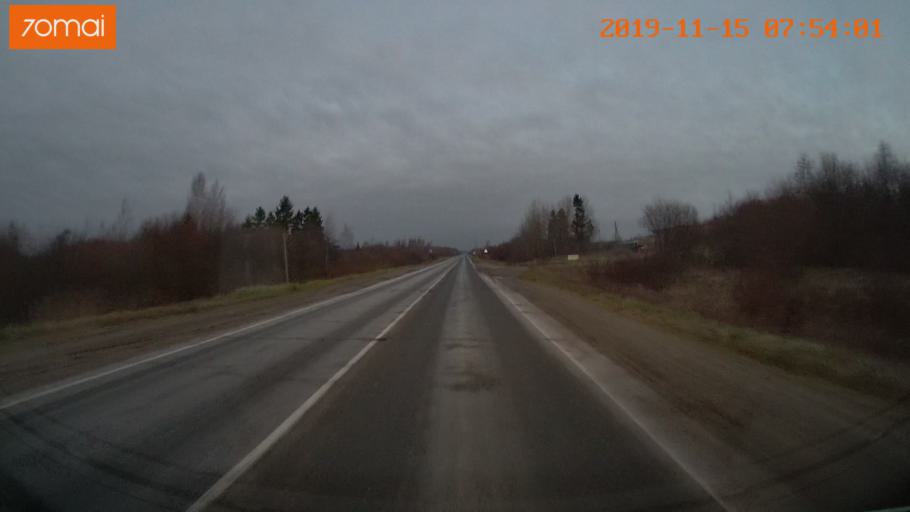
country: RU
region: Vologda
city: Cherepovets
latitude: 58.8947
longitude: 38.1805
